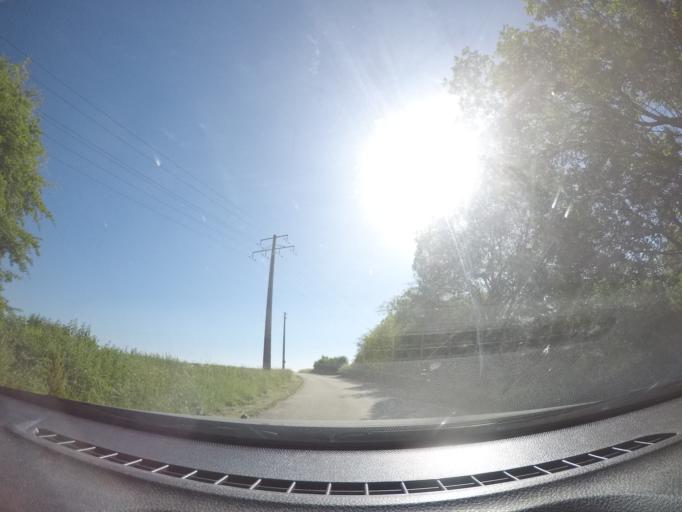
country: BE
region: Wallonia
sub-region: Province de Namur
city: Philippeville
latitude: 50.1837
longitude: 4.5875
